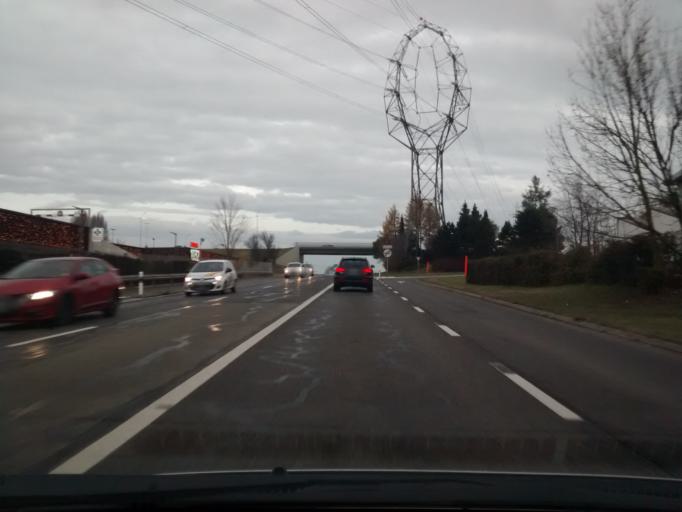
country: CH
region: Vaud
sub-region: Lausanne District
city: Romanel
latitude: 46.5592
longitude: 6.6141
